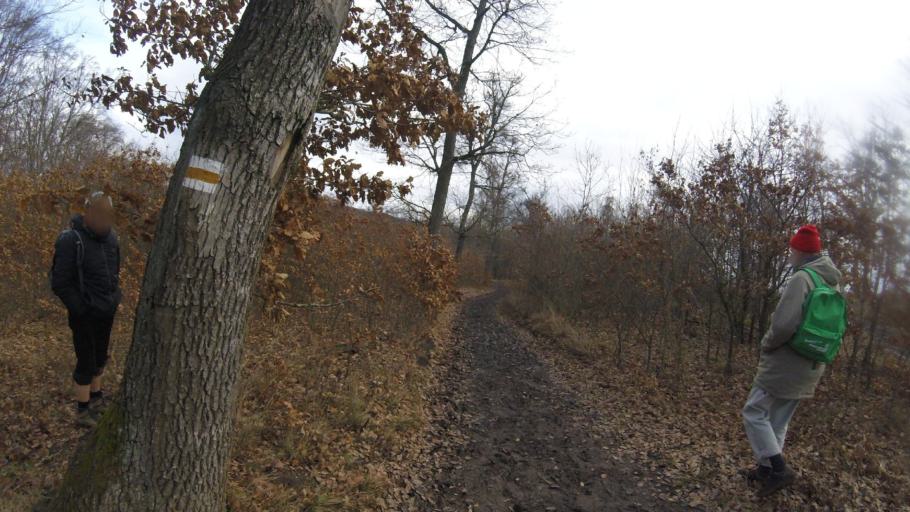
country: HU
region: Pest
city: Nagykovacsi
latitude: 47.6815
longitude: 19.0009
